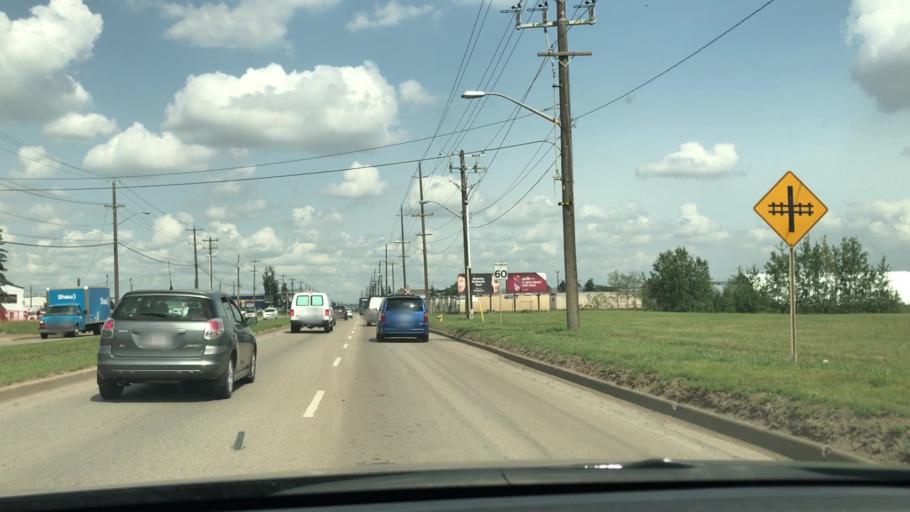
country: CA
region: Alberta
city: Edmonton
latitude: 53.5058
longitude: -113.4181
